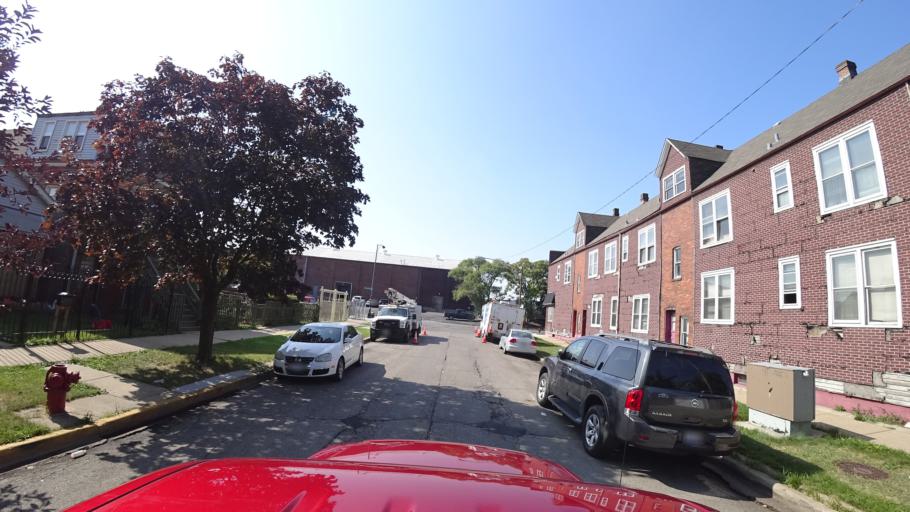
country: US
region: Illinois
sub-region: Cook County
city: Cicero
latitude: 41.8231
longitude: -87.7069
